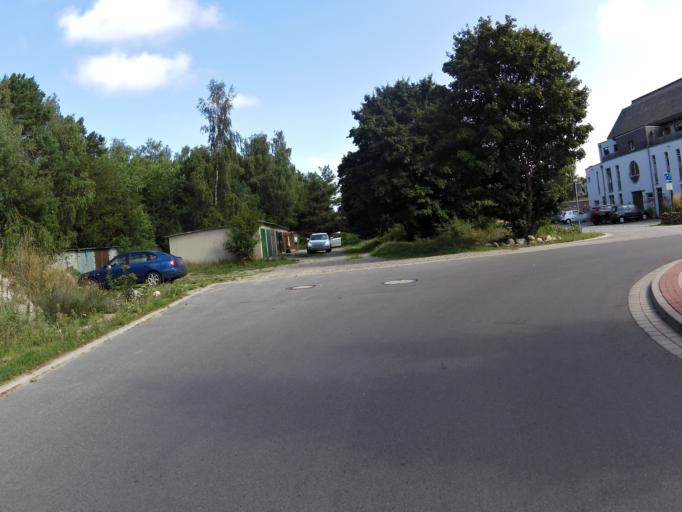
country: DE
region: Mecklenburg-Vorpommern
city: Karlshagen
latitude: 54.1226
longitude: 13.8306
